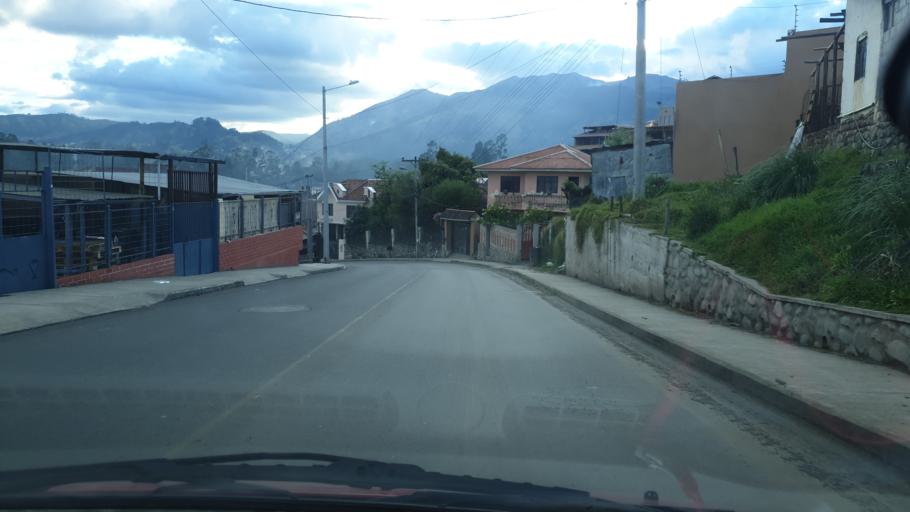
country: EC
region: Azuay
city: Cuenca
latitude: -2.8837
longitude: -79.0423
